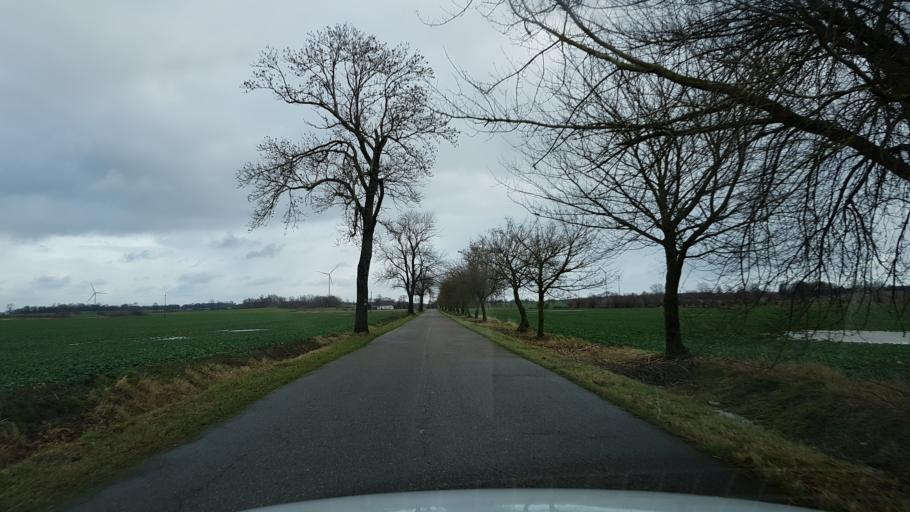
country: PL
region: West Pomeranian Voivodeship
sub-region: Powiat slawienski
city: Slawno
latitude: 54.5178
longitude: 16.6779
